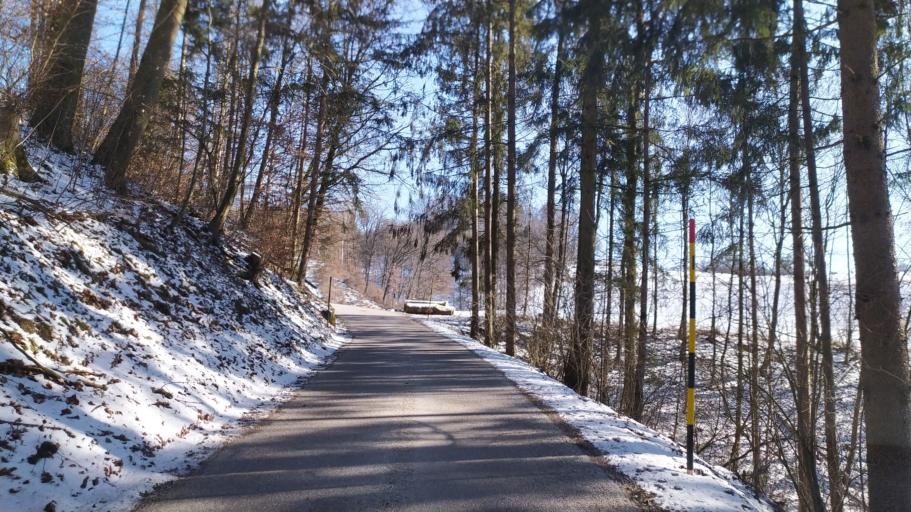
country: AT
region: Upper Austria
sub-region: Politischer Bezirk Urfahr-Umgebung
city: Ottensheim
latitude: 48.3314
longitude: 14.2009
